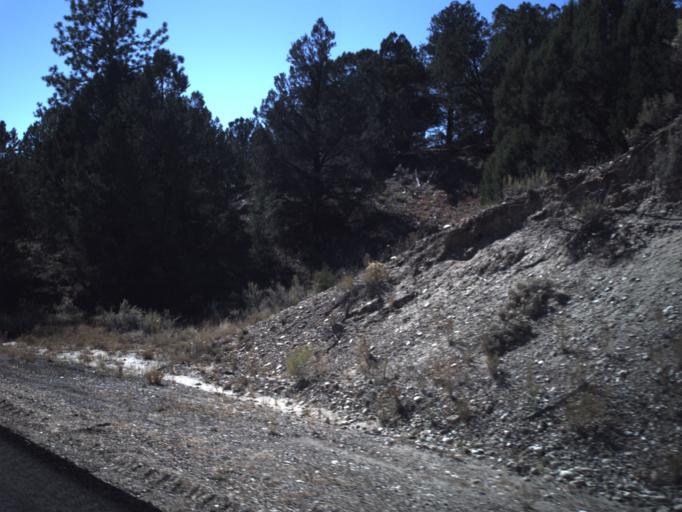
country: US
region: Utah
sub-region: Garfield County
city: Panguitch
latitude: 37.7012
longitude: -111.7911
